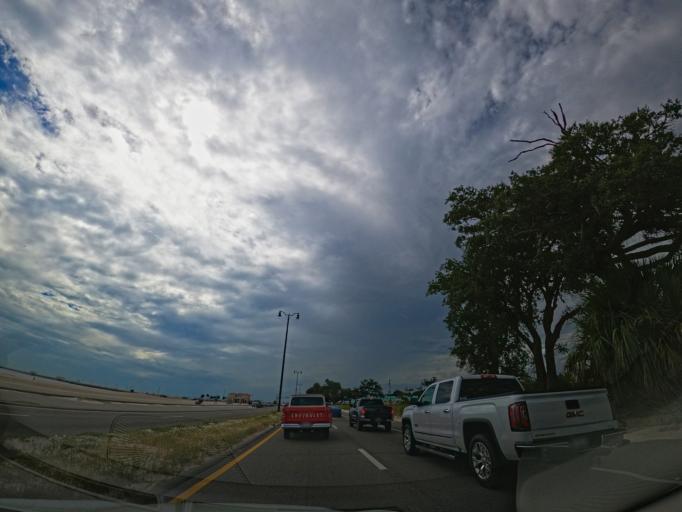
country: US
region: Mississippi
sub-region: Harrison County
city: Gulfport
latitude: 30.3795
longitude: -89.0411
